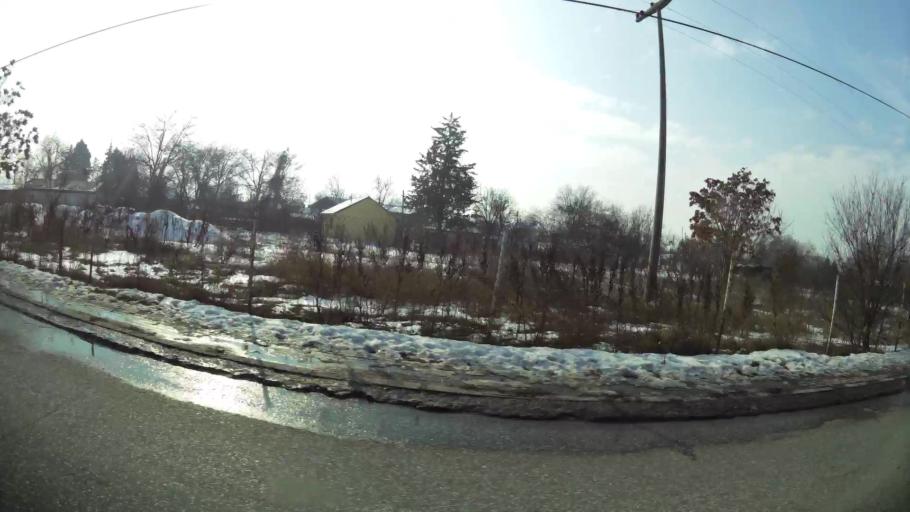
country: MK
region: Suto Orizari
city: Suto Orizare
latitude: 42.0156
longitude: 21.3931
